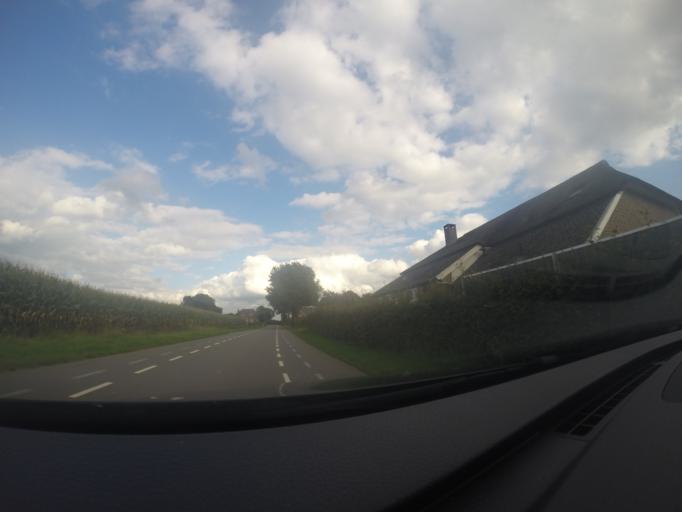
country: NL
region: Gelderland
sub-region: Gemeente Doesburg
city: Doesburg
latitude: 52.0278
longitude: 6.1929
